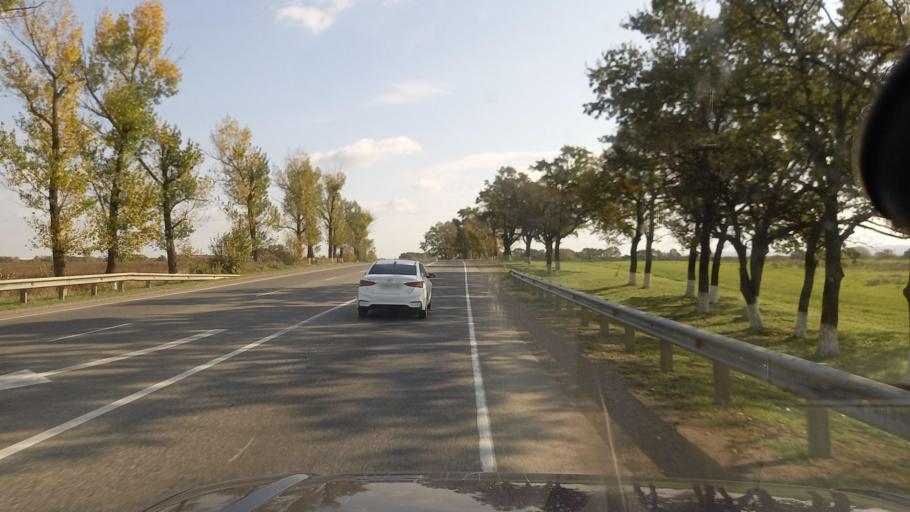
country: RU
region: Krasnodarskiy
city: Akhtyrskiy
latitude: 44.8543
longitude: 38.3401
